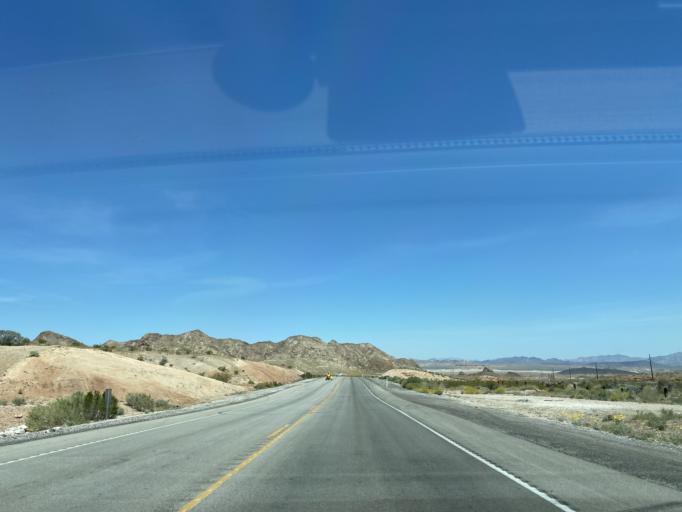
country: US
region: Nevada
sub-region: Clark County
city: Nellis Air Force Base
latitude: 36.2062
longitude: -114.9622
